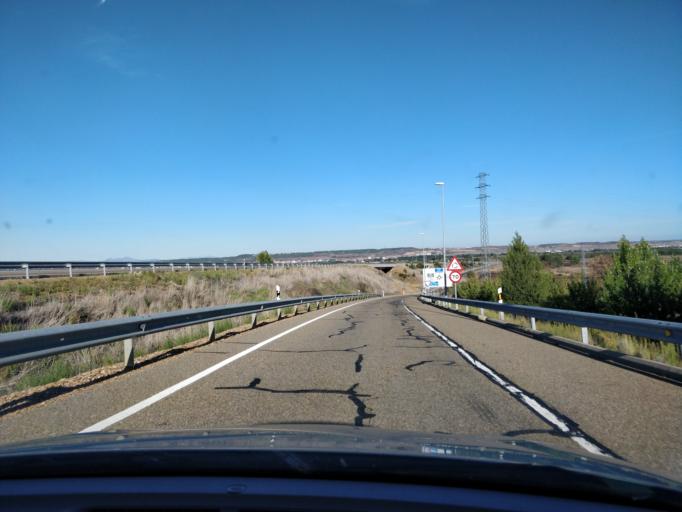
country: ES
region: Castille and Leon
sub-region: Provincia de Leon
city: San Andres del Rabanedo
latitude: 42.5763
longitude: -5.6241
